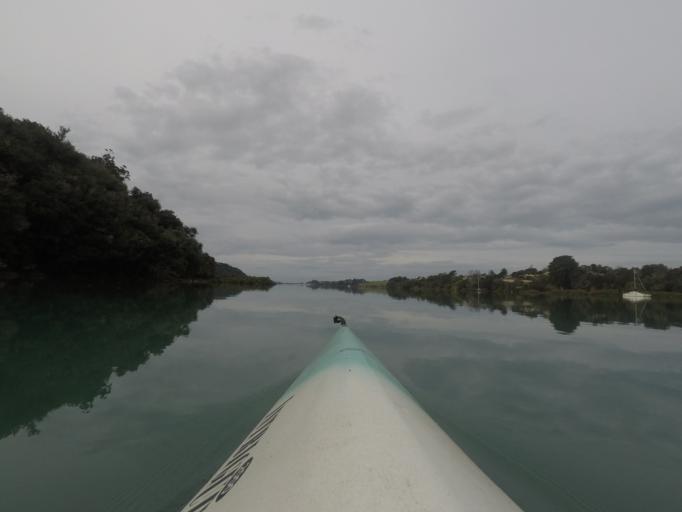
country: NZ
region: Auckland
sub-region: Auckland
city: Rothesay Bay
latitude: -36.6741
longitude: 174.7139
